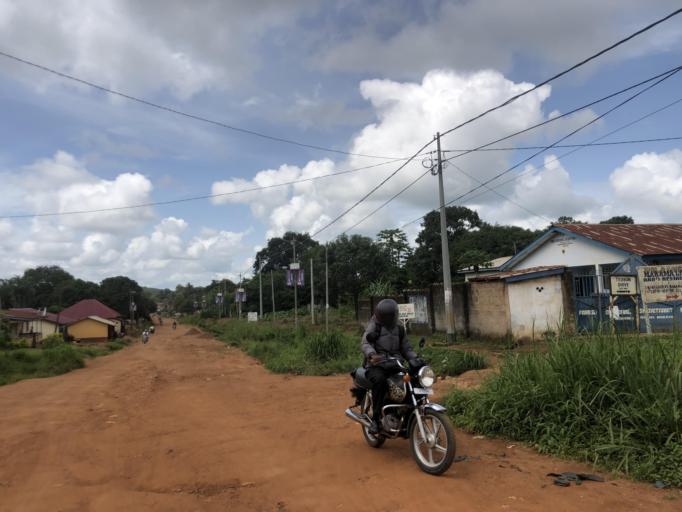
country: SL
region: Northern Province
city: Makeni
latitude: 8.8722
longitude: -12.0523
